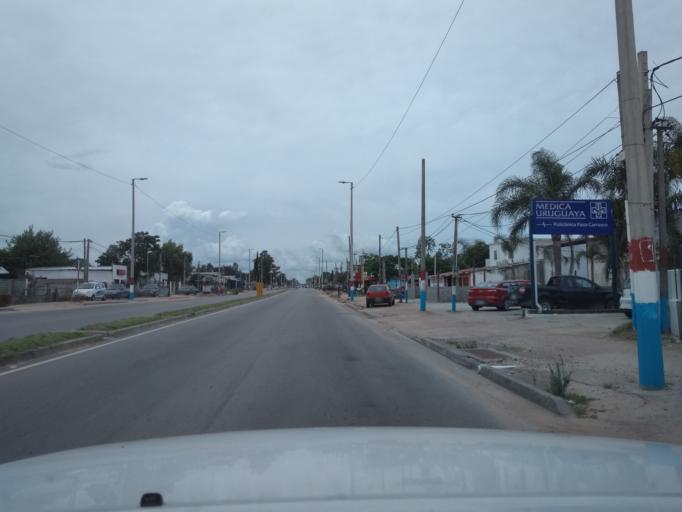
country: UY
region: Canelones
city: Paso de Carrasco
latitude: -34.8642
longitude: -56.0572
